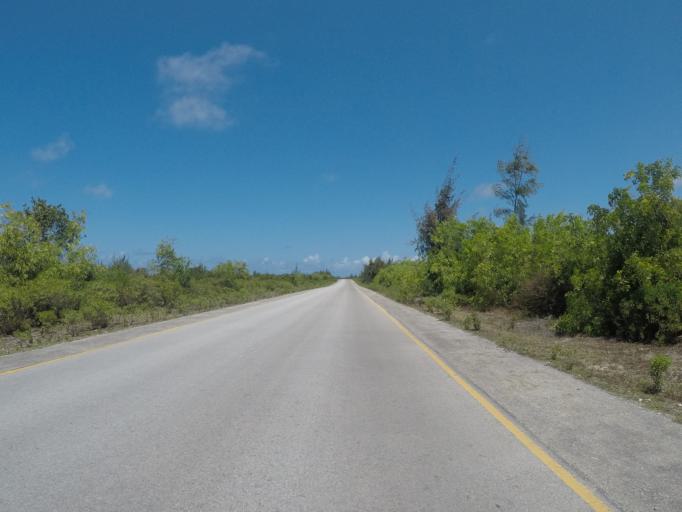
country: TZ
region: Zanzibar Central/South
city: Nganane
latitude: -6.4009
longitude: 39.5615
